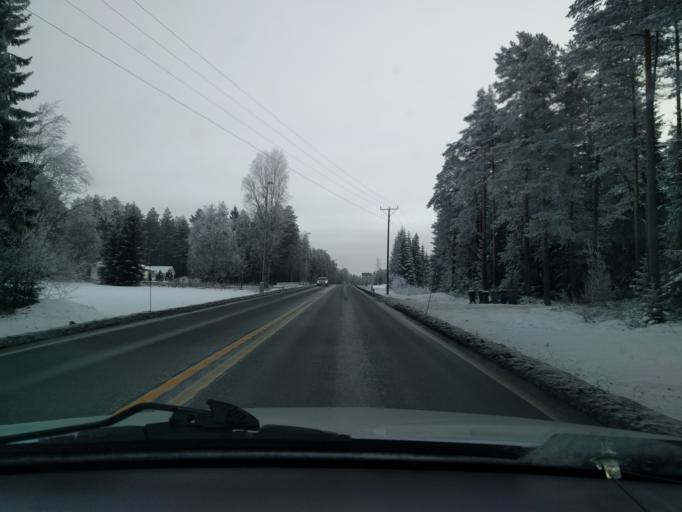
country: NO
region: Hedmark
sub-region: Loten
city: Loten
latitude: 60.8574
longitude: 11.3943
